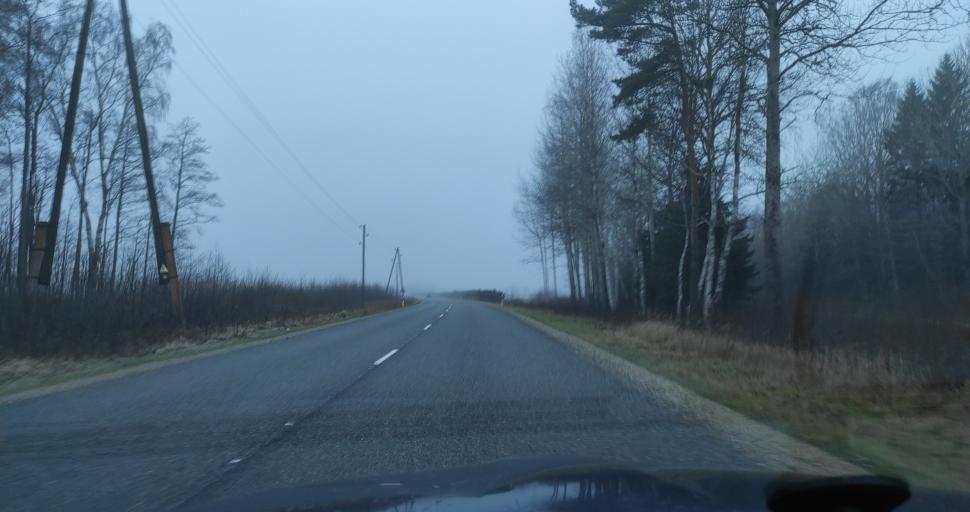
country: LV
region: Alsunga
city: Alsunga
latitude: 56.9934
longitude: 21.3684
